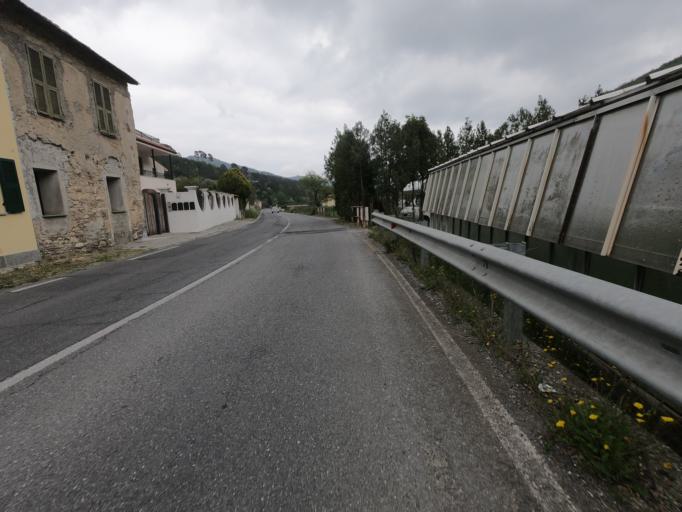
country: IT
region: Liguria
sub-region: Provincia di Savona
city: Villafranca
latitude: 44.0024
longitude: 8.1001
